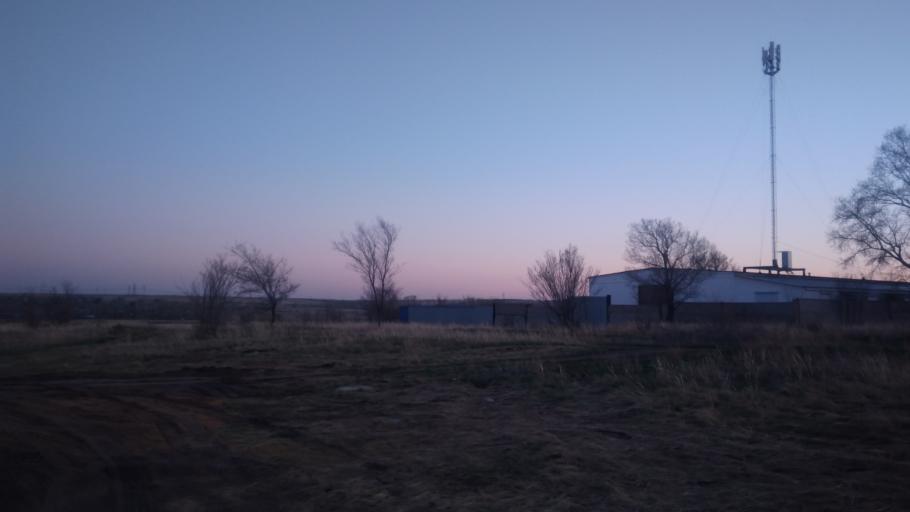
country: RU
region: Chelyabinsk
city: Troitsk
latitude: 54.0747
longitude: 61.5225
